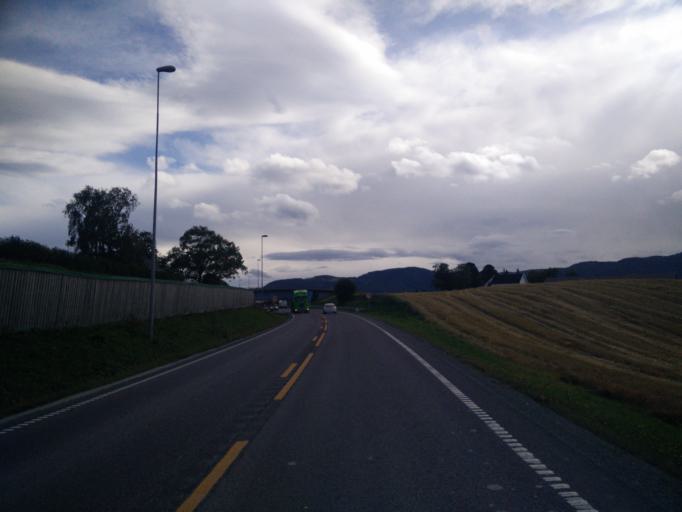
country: NO
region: Sor-Trondelag
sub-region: Melhus
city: Melhus
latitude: 63.3243
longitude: 10.2922
